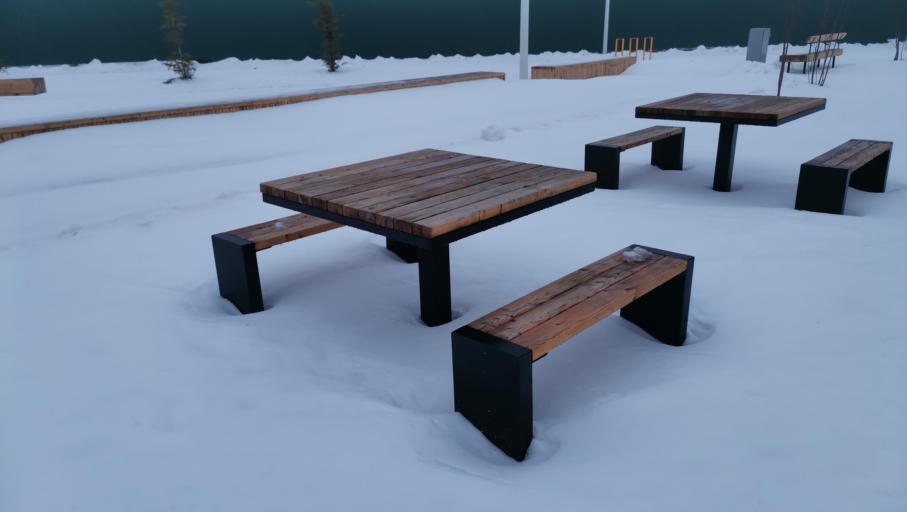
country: RU
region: Tatarstan
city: Sviyazhsk
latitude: 55.7448
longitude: 48.7475
